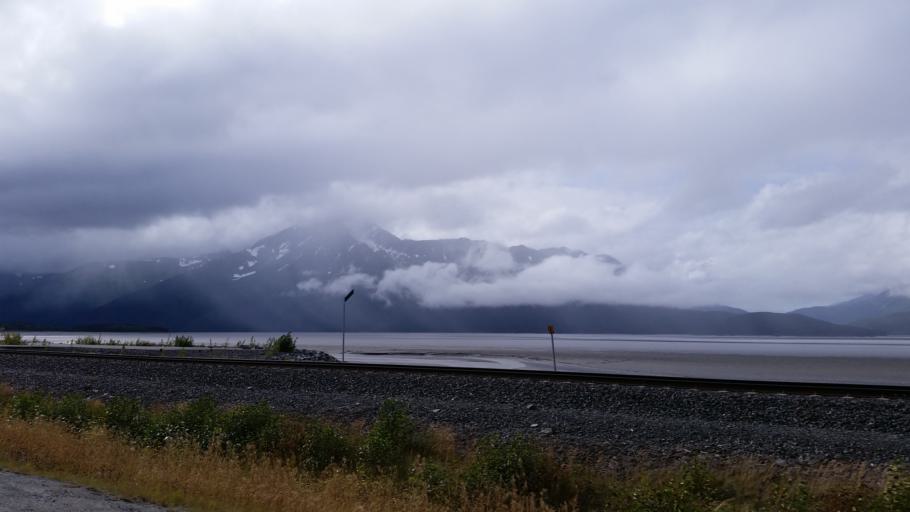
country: US
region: Alaska
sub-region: Anchorage Municipality
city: Girdwood
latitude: 60.9502
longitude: -149.3982
